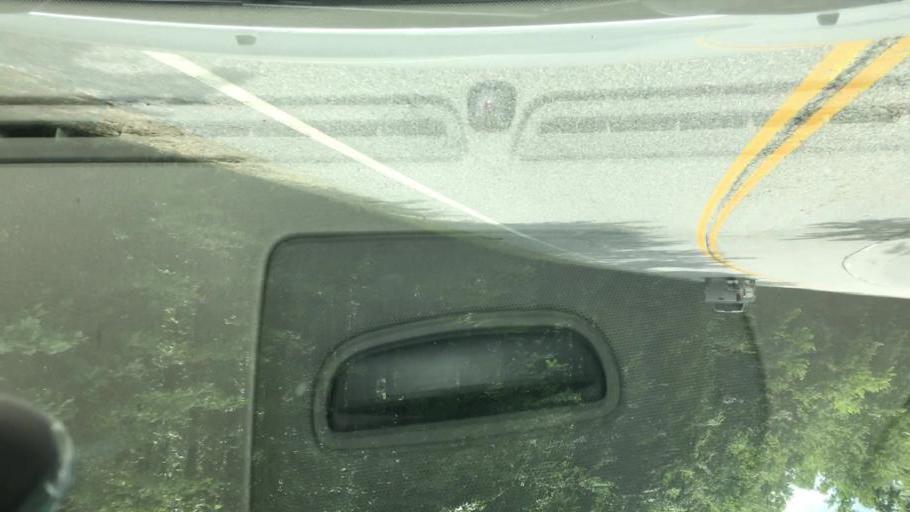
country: US
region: Georgia
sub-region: Union County
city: Blairsville
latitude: 34.7012
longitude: -83.9159
